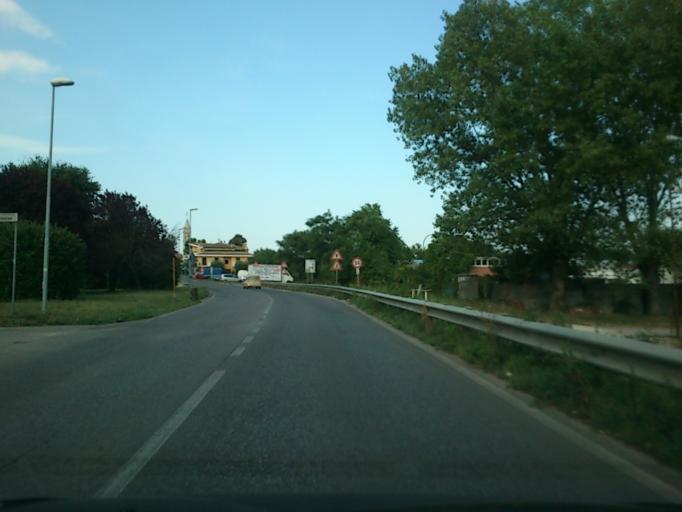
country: IT
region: The Marches
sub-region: Provincia di Pesaro e Urbino
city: Rosciano
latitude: 43.8164
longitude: 12.9897
